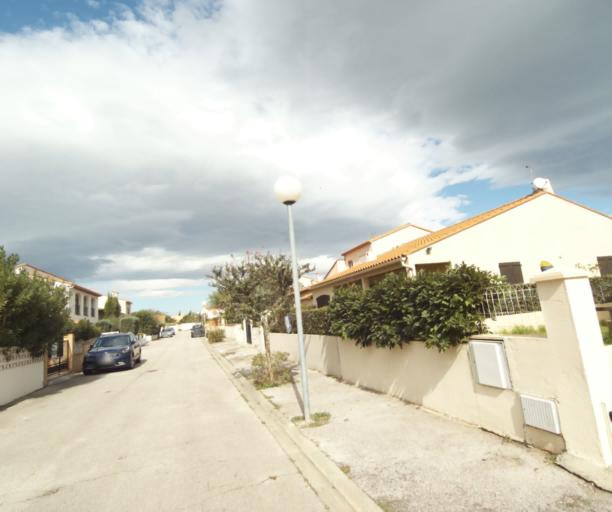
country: FR
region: Languedoc-Roussillon
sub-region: Departement des Pyrenees-Orientales
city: Argelers
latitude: 42.5524
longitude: 3.0253
